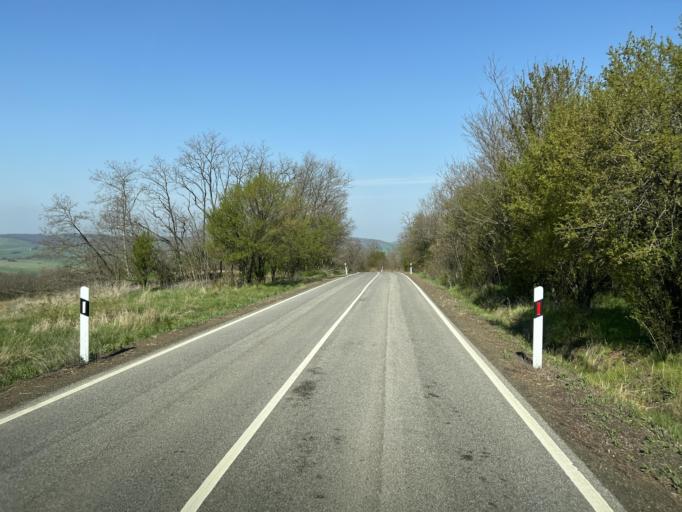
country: HU
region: Pest
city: Szob
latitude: 47.9390
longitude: 18.7862
